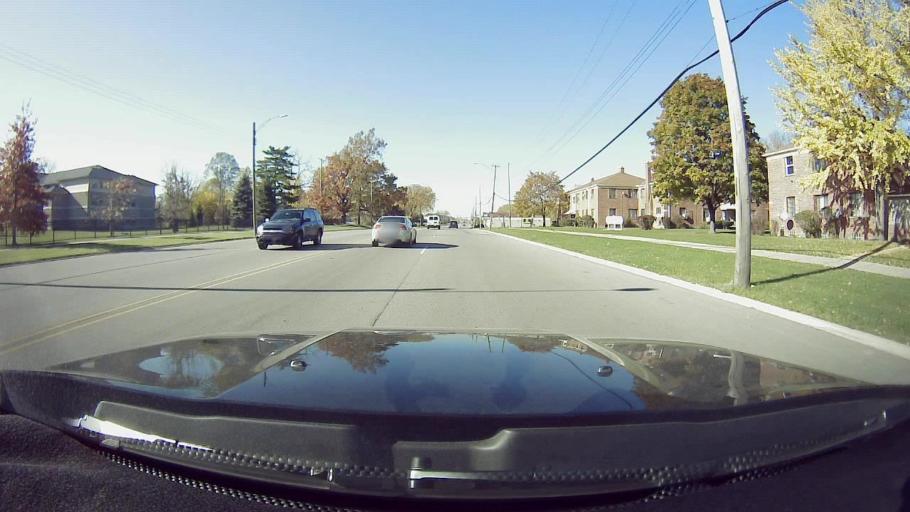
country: US
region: Michigan
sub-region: Wayne County
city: Dearborn
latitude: 42.3581
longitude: -83.2020
